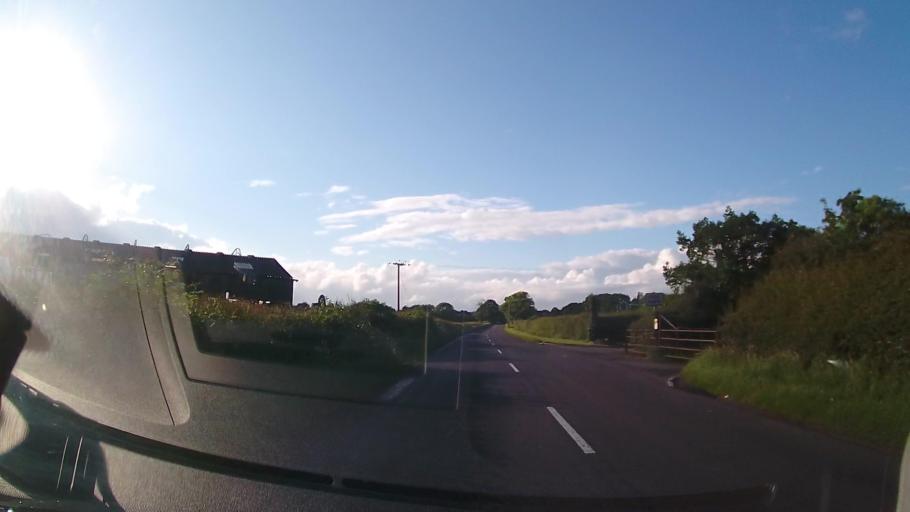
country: GB
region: England
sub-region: Leicestershire
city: Markfield
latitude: 52.6722
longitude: -1.2730
